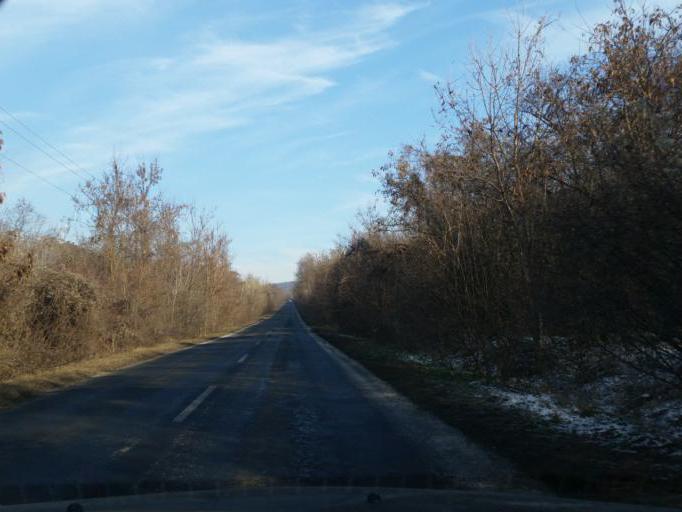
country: HU
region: Pest
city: Paty
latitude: 47.5310
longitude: 18.8392
